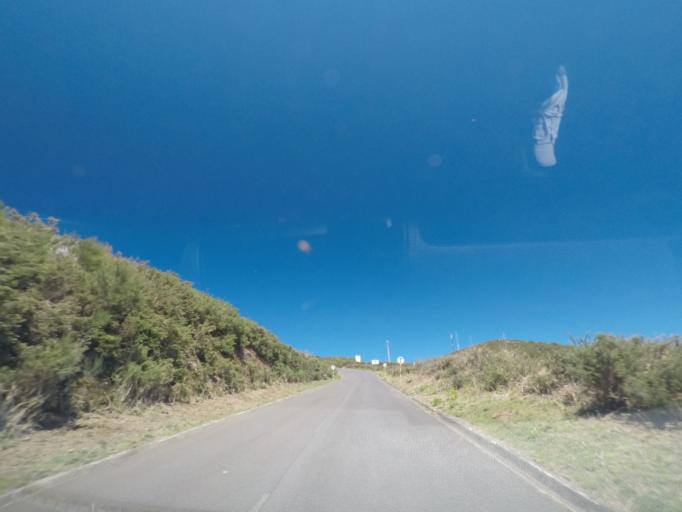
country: PT
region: Madeira
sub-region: Calheta
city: Arco da Calheta
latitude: 32.7496
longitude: -17.1242
